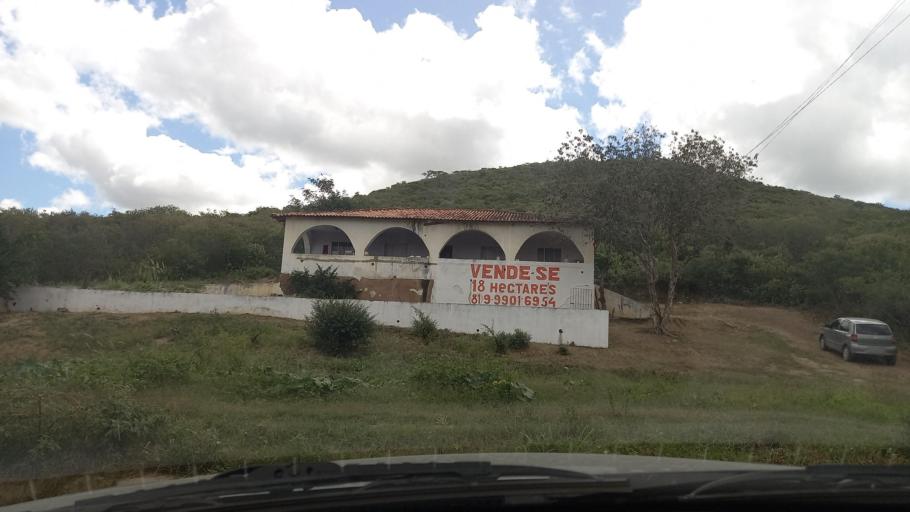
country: BR
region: Pernambuco
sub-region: Caruaru
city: Caruaru
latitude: -8.2759
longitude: -35.9397
